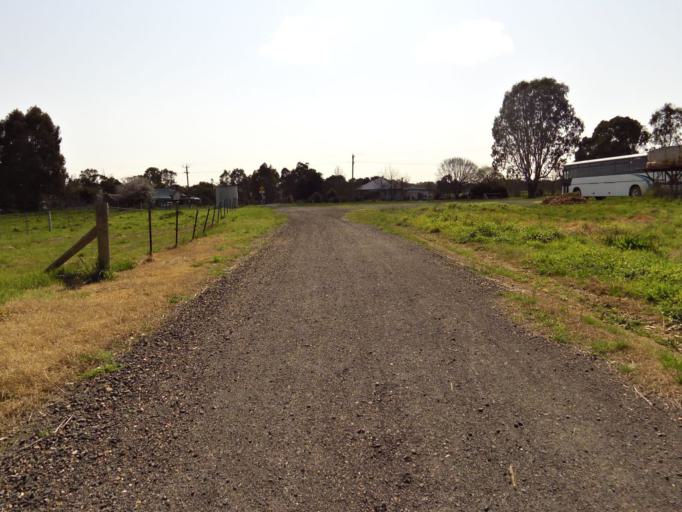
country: AU
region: Victoria
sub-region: Murrindindi
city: Alexandra
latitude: -37.1022
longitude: 145.6183
